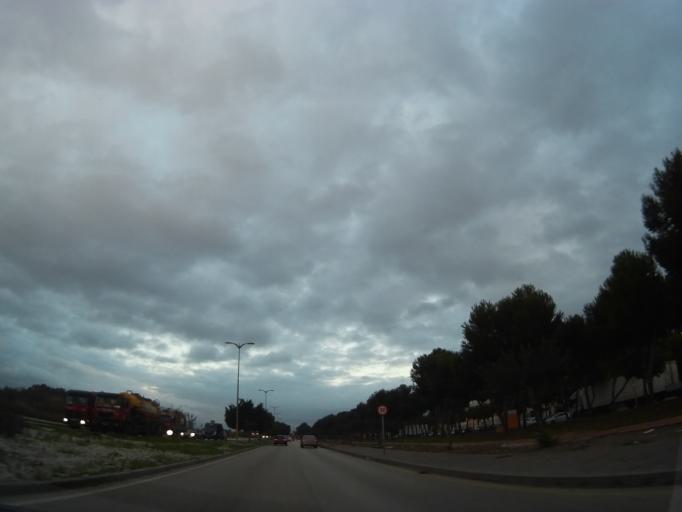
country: ES
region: Andalusia
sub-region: Provincia de Malaga
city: Malaga
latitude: 36.6862
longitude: -4.4749
